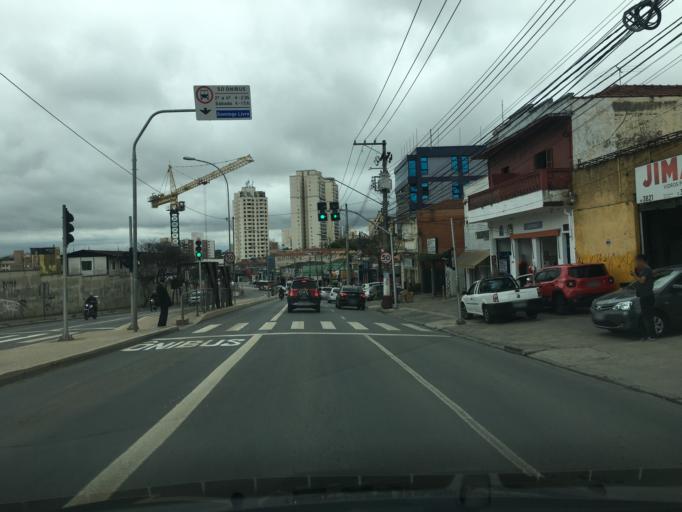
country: BR
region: Sao Paulo
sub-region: Taboao Da Serra
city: Taboao da Serra
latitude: -23.5929
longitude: -46.7335
